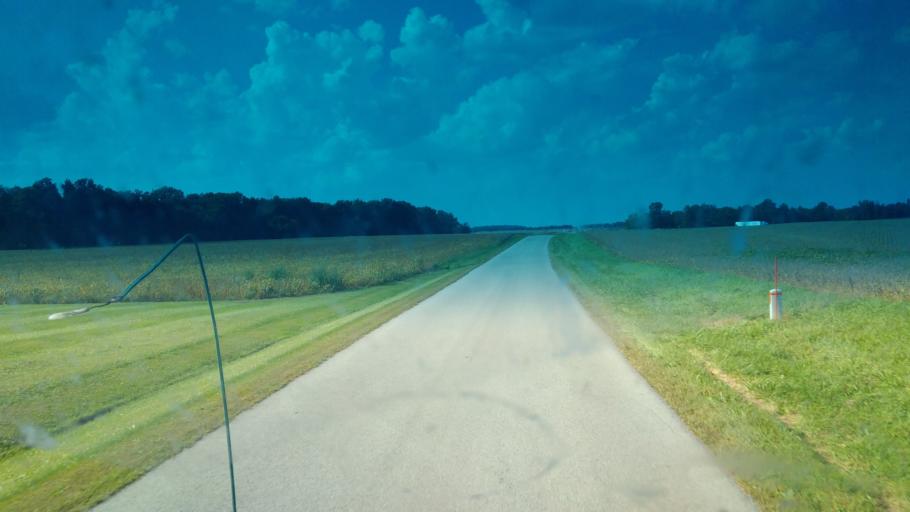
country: US
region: Ohio
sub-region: Hardin County
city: Forest
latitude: 40.8222
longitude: -83.5586
